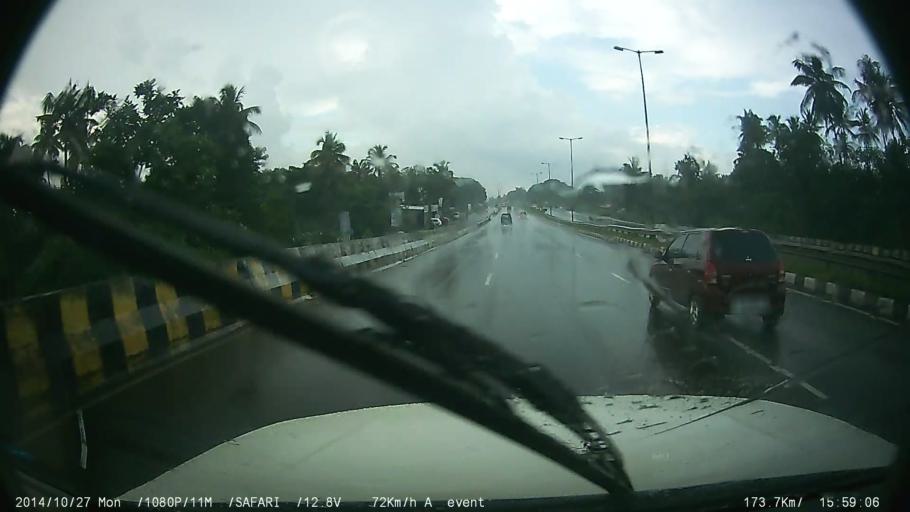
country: IN
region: Kerala
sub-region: Thrissur District
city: Kizhake Chalakudi
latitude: 10.3033
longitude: 76.3361
